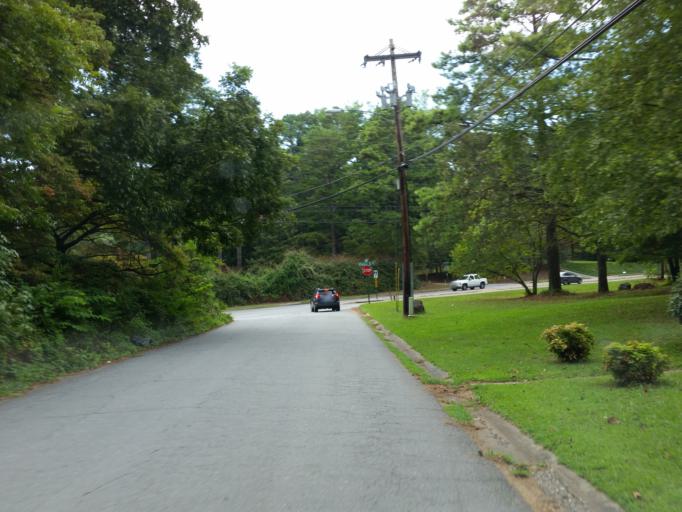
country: US
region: Georgia
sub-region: Cobb County
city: Marietta
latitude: 34.0152
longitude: -84.5371
